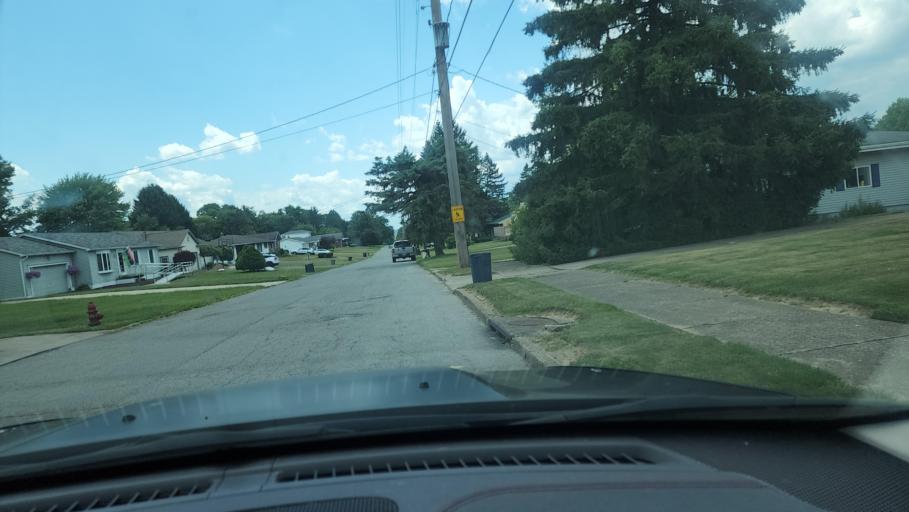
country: US
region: Ohio
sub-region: Mahoning County
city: Campbell
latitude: 41.0786
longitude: -80.5793
